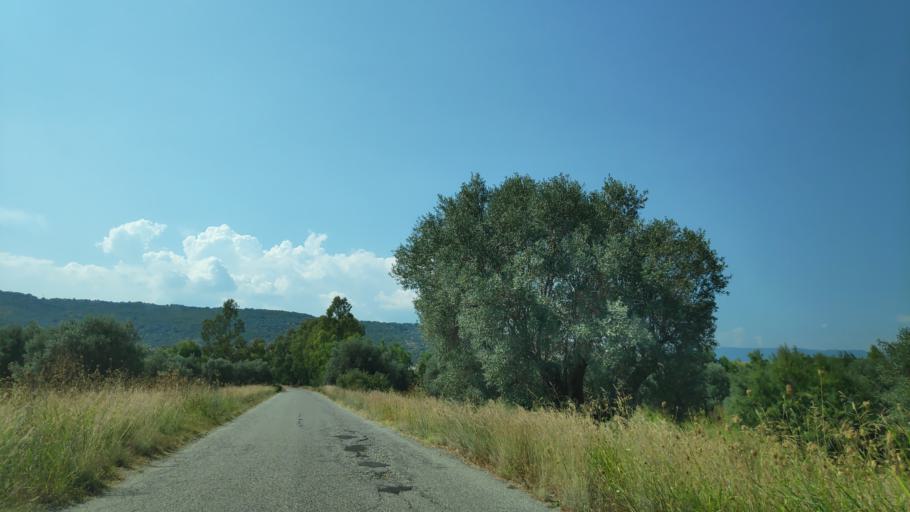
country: IT
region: Calabria
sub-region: Provincia di Reggio Calabria
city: Monasterace
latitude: 38.4265
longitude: 16.5318
